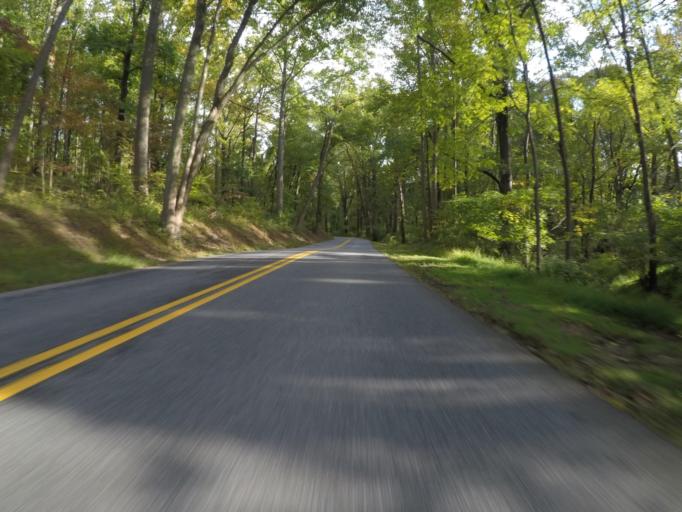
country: US
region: Maryland
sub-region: Baltimore County
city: Reisterstown
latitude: 39.5249
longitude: -76.7766
